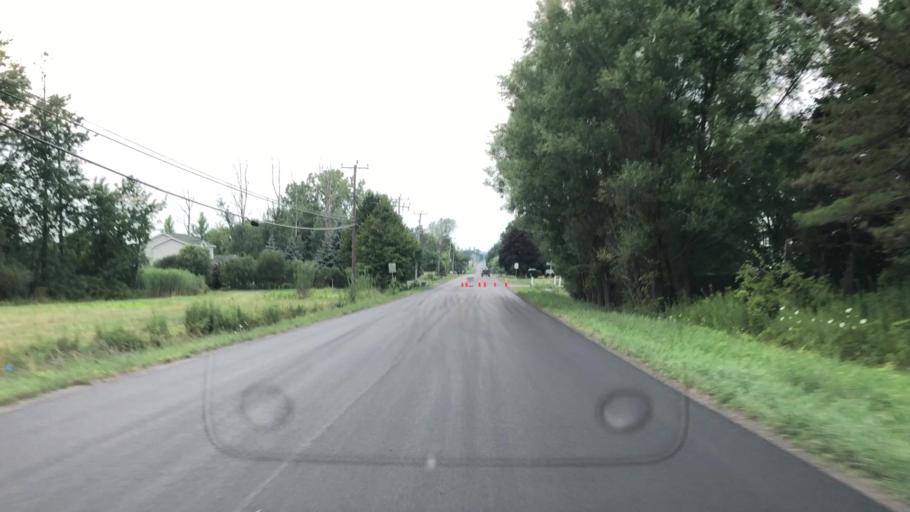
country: US
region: New York
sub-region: Erie County
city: Elma Center
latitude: 42.8254
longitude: -78.6059
